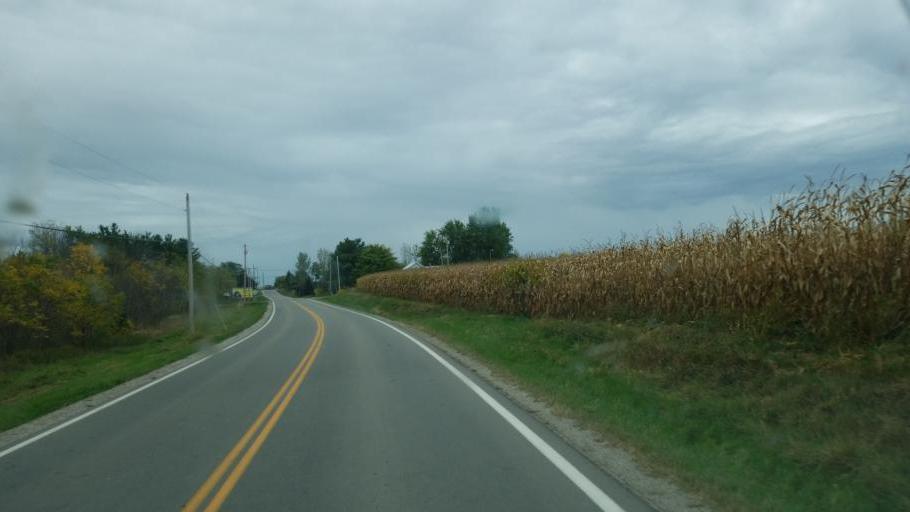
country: US
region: Ohio
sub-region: Huron County
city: New London
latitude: 41.1176
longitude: -82.4096
